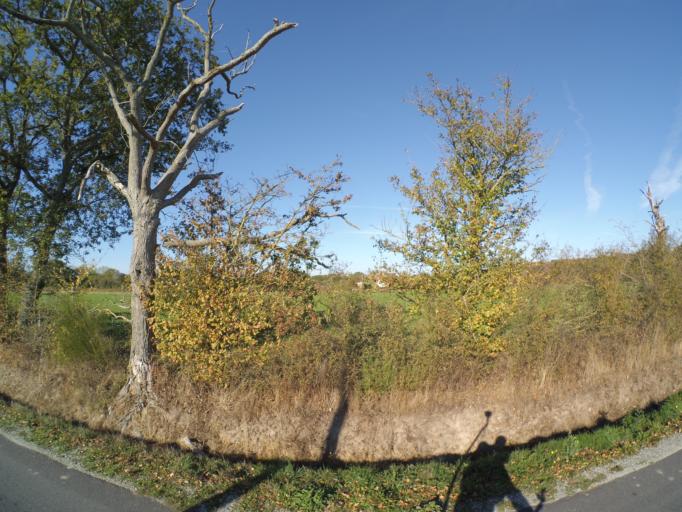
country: FR
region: Pays de la Loire
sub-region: Departement de la Loire-Atlantique
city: Saint-Lumine-de-Clisson
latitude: 47.0814
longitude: -1.3289
